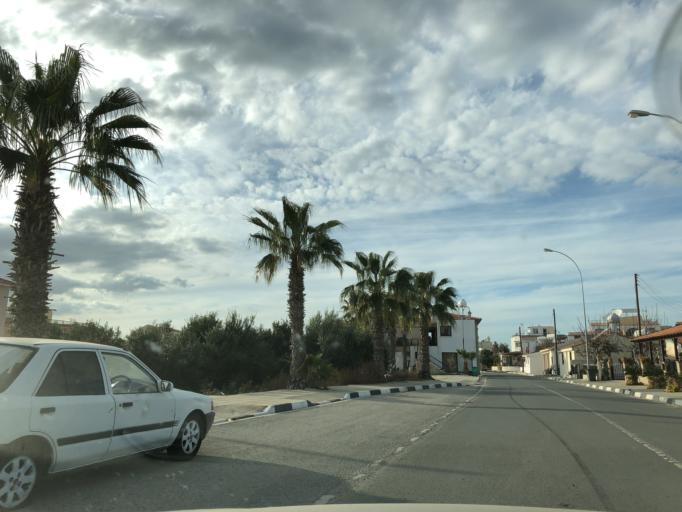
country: CY
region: Larnaka
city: Perivolia
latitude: 34.8273
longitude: 33.5823
